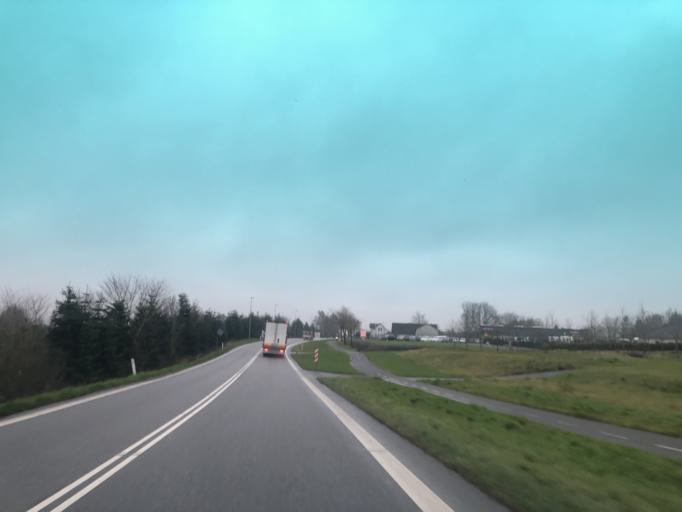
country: DK
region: South Denmark
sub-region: Nyborg Kommune
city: Ullerslev
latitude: 55.2663
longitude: 10.6751
